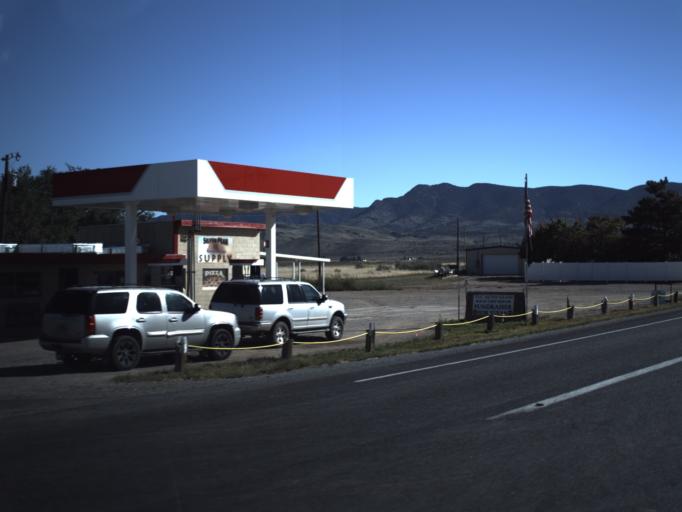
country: US
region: Utah
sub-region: Washington County
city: Enterprise
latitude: 37.6721
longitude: -113.5491
